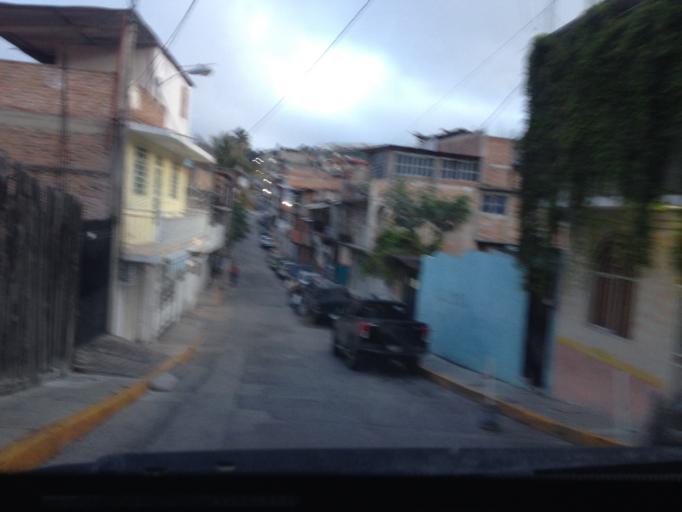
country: MX
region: Guerrero
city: Chilpancingo de los Bravos
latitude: 17.5590
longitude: -99.5008
